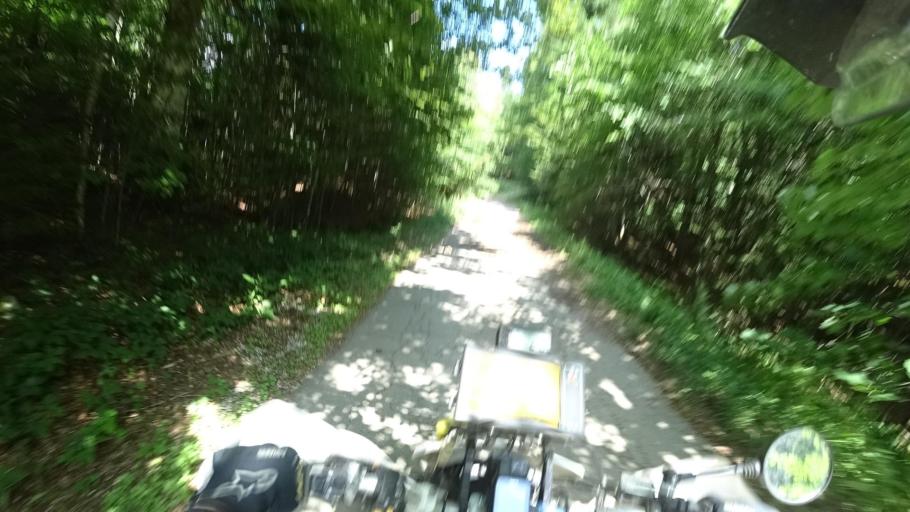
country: HR
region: Licko-Senjska
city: Brinje
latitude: 45.1245
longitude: 15.0412
